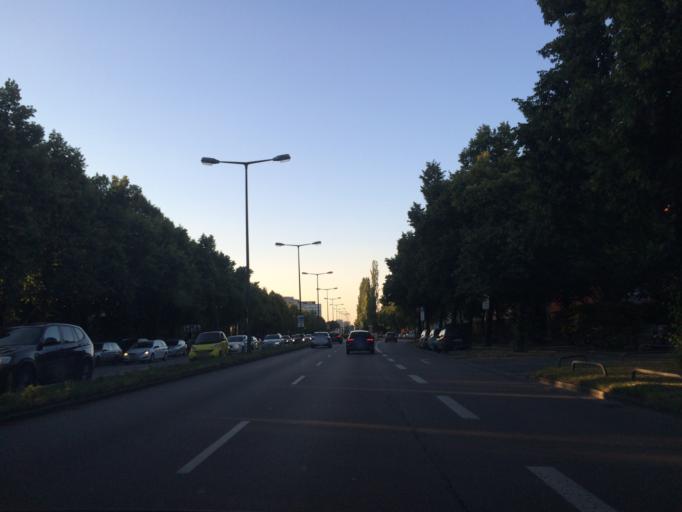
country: DE
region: Bavaria
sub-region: Upper Bavaria
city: Munich
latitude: 48.1612
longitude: 11.5377
